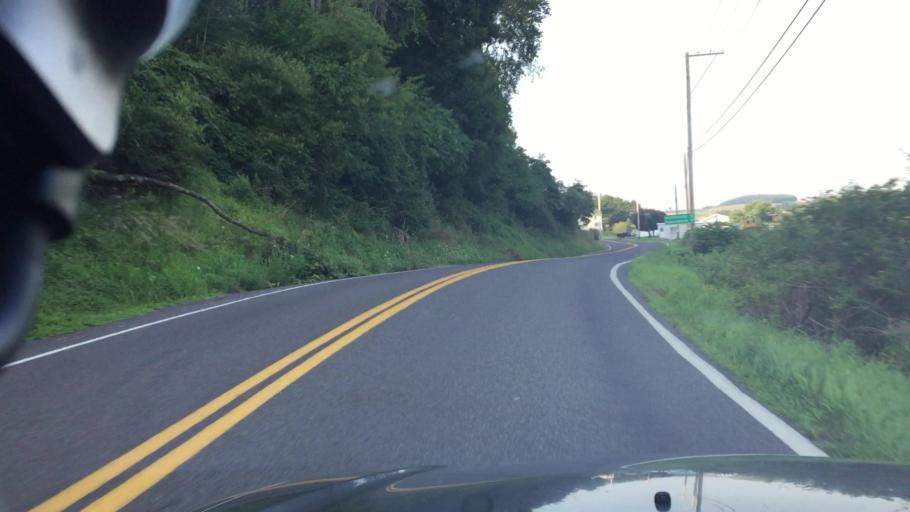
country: US
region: Pennsylvania
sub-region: Columbia County
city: Almedia
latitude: 40.9789
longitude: -76.3694
